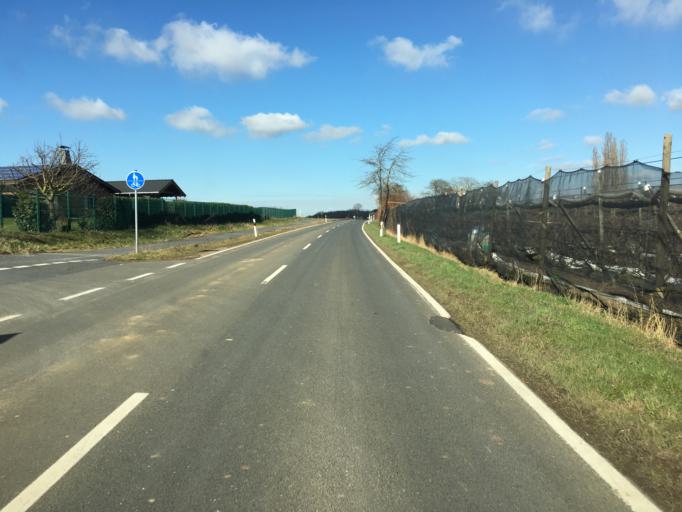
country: DE
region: North Rhine-Westphalia
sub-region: Regierungsbezirk Koln
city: Mechernich
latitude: 50.6182
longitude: 6.6390
